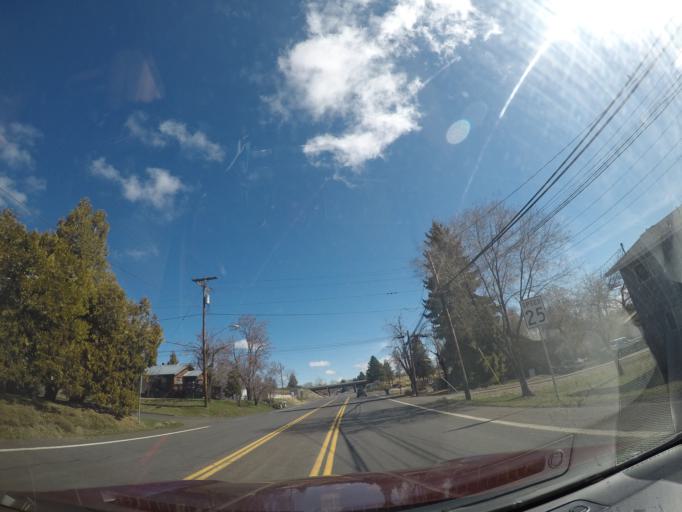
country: US
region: Oregon
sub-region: Klamath County
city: Klamath Falls
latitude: 42.2396
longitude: -121.7991
